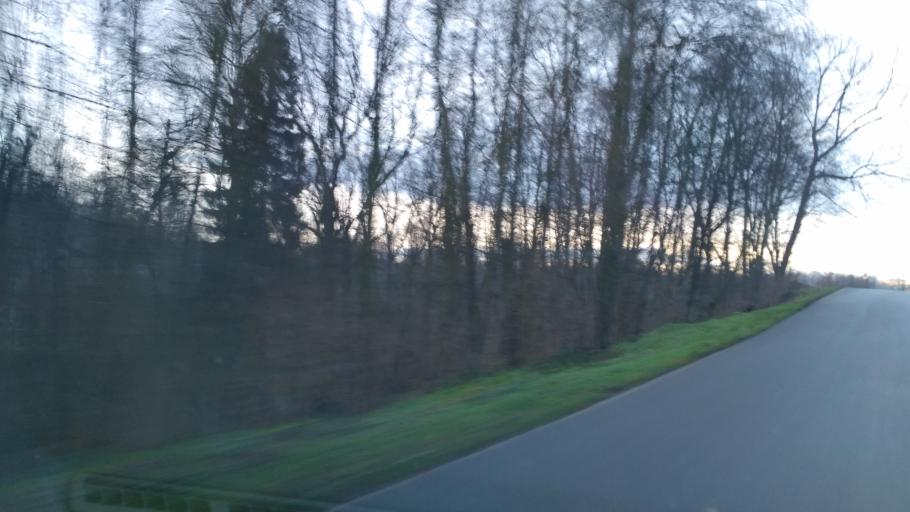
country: PL
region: Subcarpathian Voivodeship
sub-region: Powiat strzyzowski
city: Niebylec
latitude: 49.8709
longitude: 21.8800
